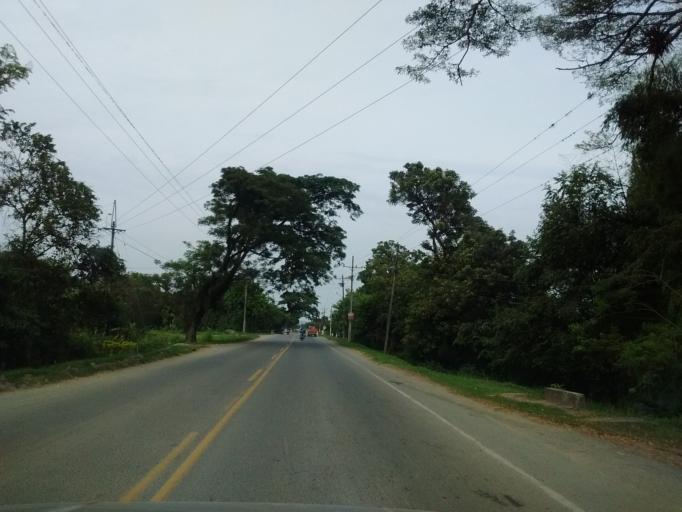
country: CO
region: Cauca
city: Puerto Tejada
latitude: 3.1808
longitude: -76.4531
